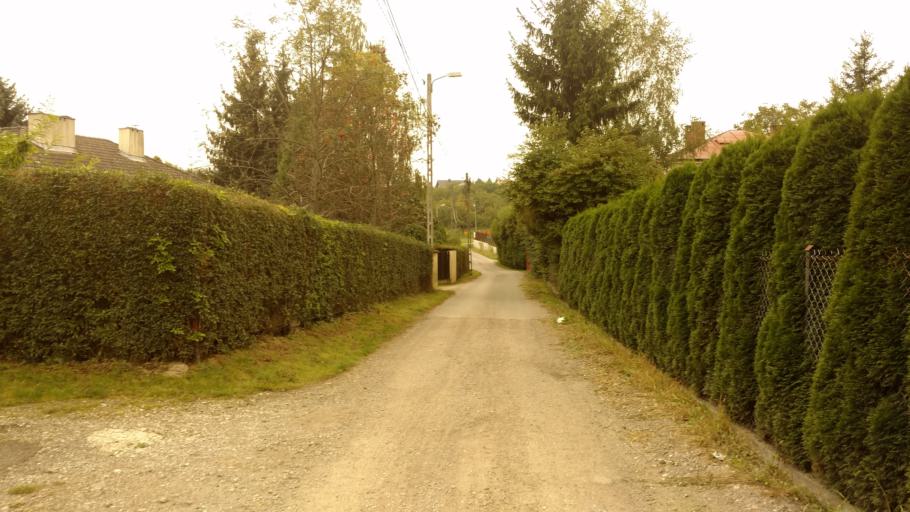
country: PL
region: Lesser Poland Voivodeship
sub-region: Powiat krakowski
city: Michalowice
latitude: 50.1365
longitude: 19.9708
